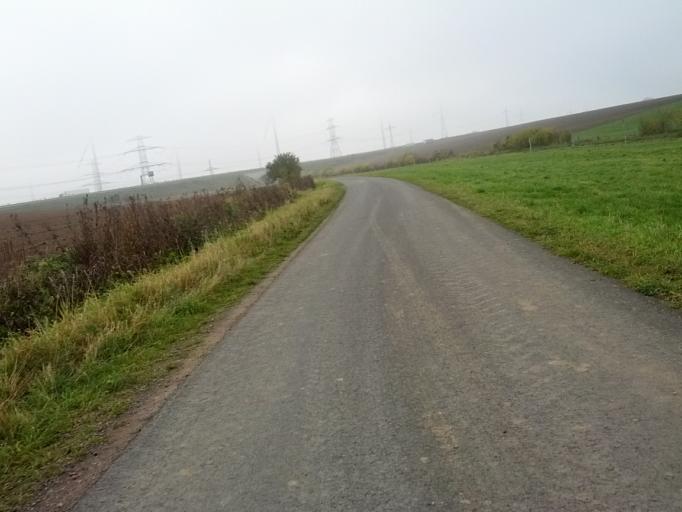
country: DE
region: Thuringia
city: Bischofroda
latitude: 51.0078
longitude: 10.3982
